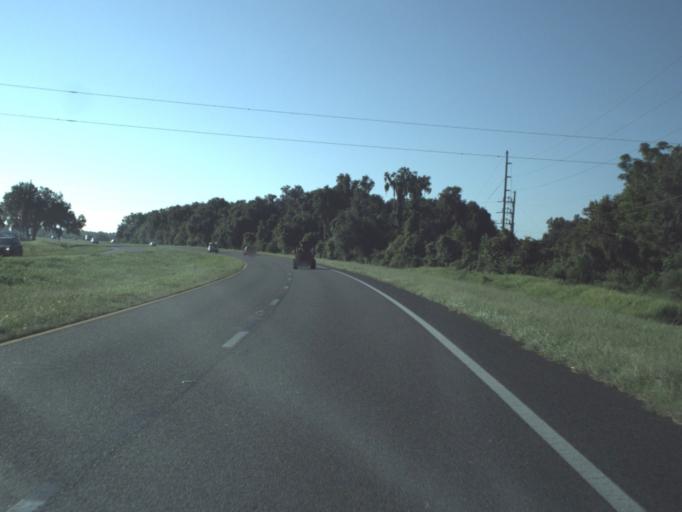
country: US
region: Florida
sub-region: Polk County
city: Fort Meade
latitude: 27.7903
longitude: -81.8142
